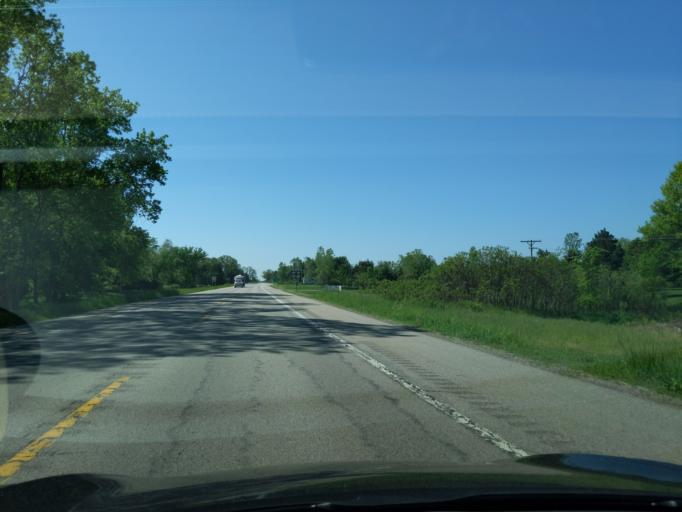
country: US
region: Michigan
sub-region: Ingham County
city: Stockbridge
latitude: 42.5146
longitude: -84.1900
